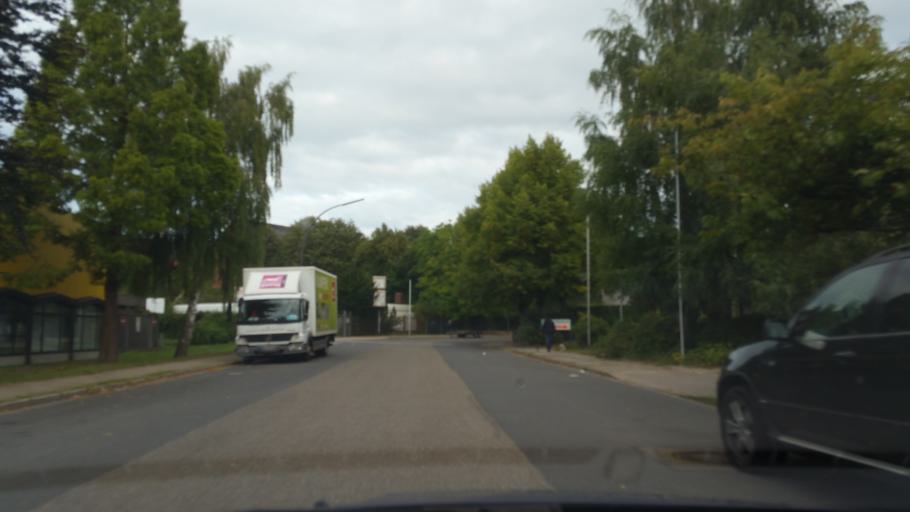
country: DE
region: Hamburg
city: Steilshoop
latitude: 53.6069
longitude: 10.0507
